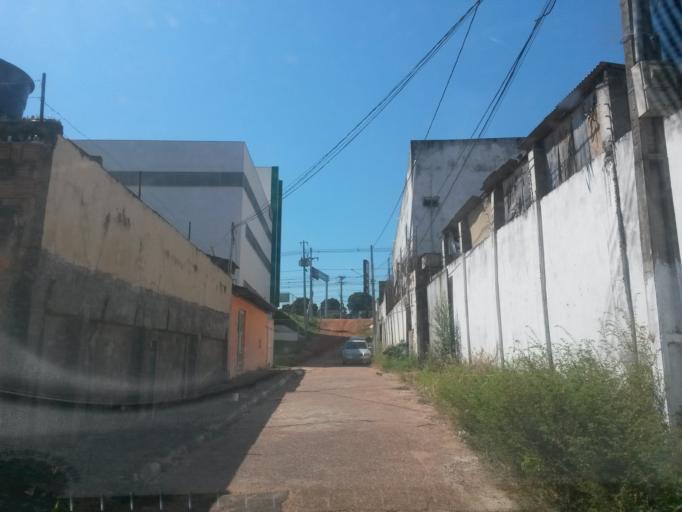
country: BR
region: Mato Grosso
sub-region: Cuiaba
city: Cuiaba
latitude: -15.5994
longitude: -56.0778
